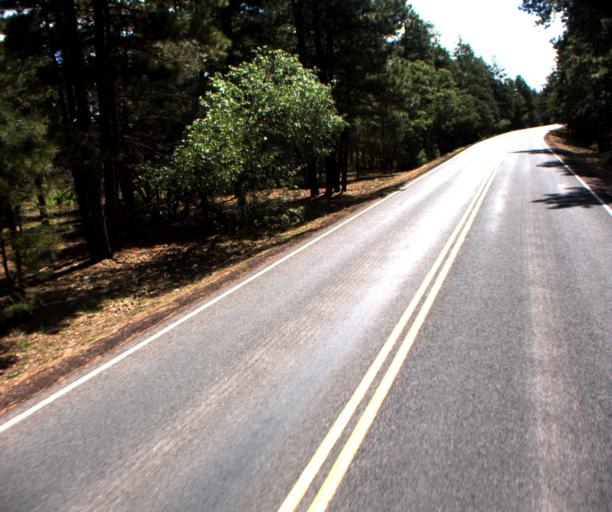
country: US
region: Arizona
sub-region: Coconino County
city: Grand Canyon
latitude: 35.9937
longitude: -112.0002
